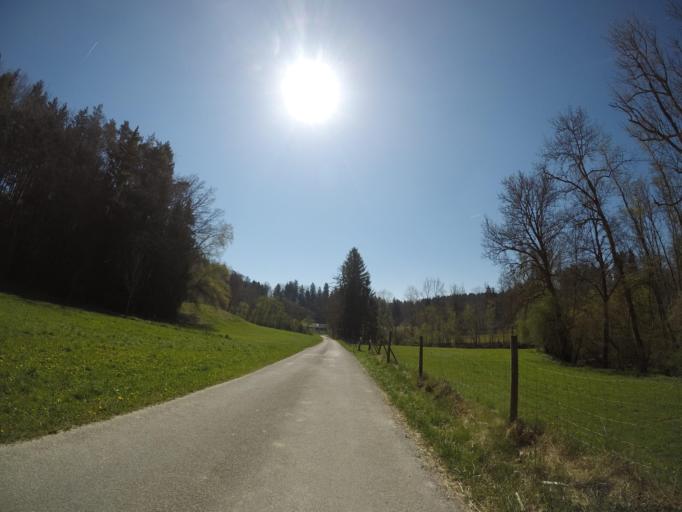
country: DE
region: Baden-Wuerttemberg
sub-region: Tuebingen Region
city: Horgenzell
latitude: 47.8193
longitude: 9.4618
